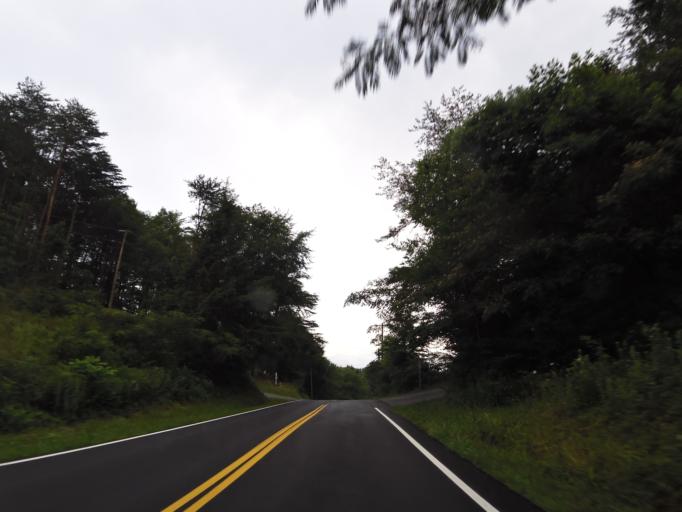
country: US
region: Tennessee
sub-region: Sevier County
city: Pigeon Forge
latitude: 35.8172
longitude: -83.6227
